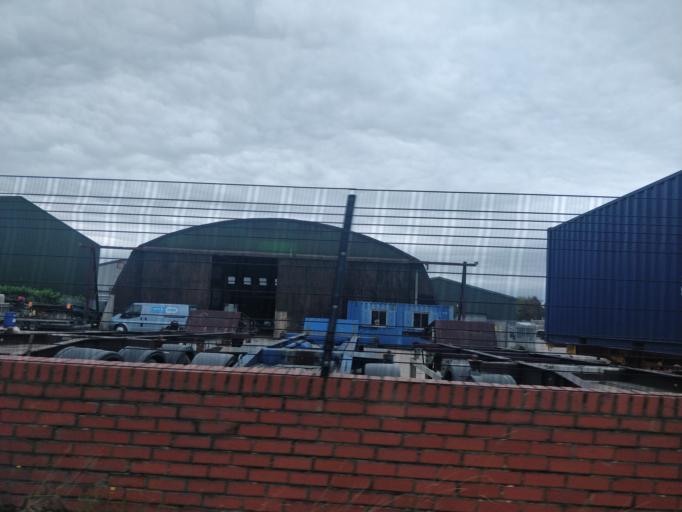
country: GB
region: England
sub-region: Lancashire
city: Ormskirk
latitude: 53.5999
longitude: -2.8654
